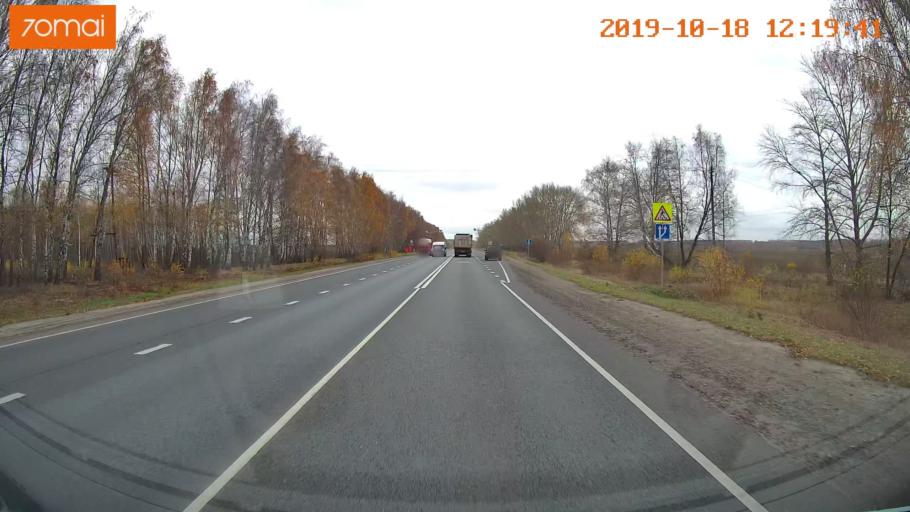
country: RU
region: Rjazan
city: Zakharovo
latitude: 54.4861
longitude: 39.4711
